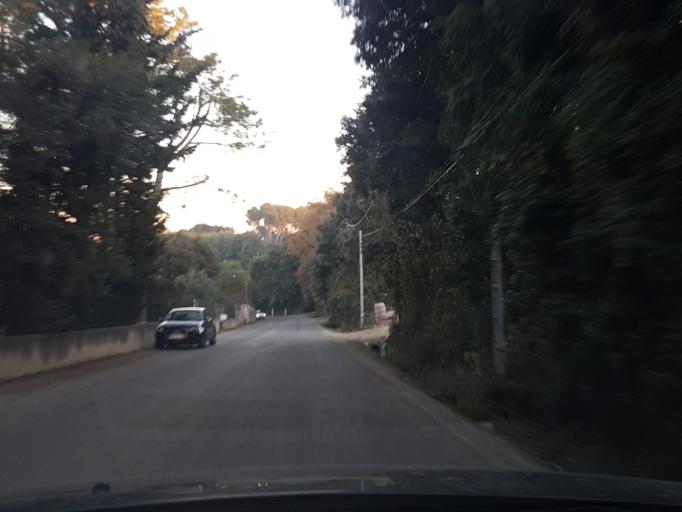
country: FR
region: Provence-Alpes-Cote d'Azur
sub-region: Departement du Vaucluse
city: Jonquerettes
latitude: 43.9467
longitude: 4.9266
